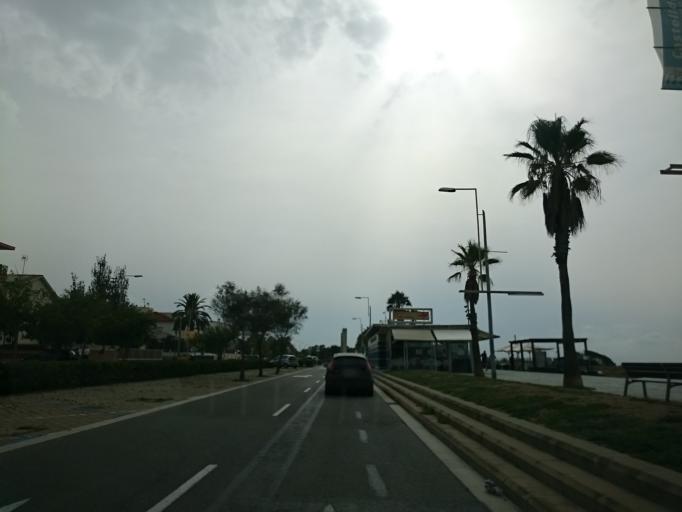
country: ES
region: Catalonia
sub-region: Provincia de Barcelona
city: Castelldefels
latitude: 41.2652
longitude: 1.9861
